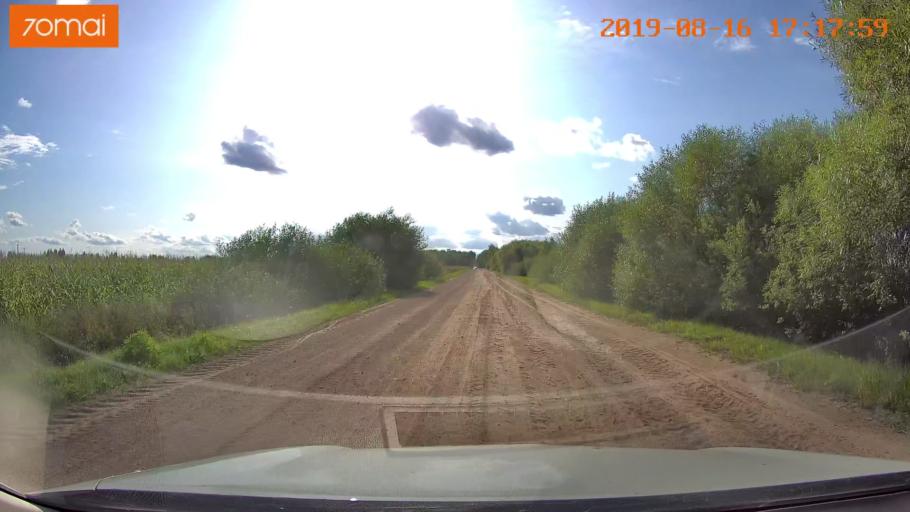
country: BY
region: Mogilev
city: Hlusha
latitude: 53.1699
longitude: 28.7981
